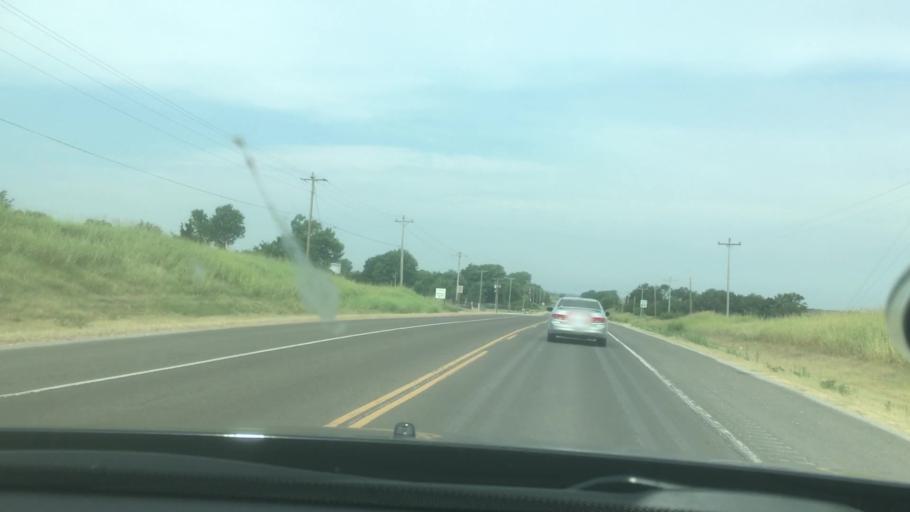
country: US
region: Oklahoma
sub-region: Garvin County
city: Maysville
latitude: 34.8192
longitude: -97.4500
